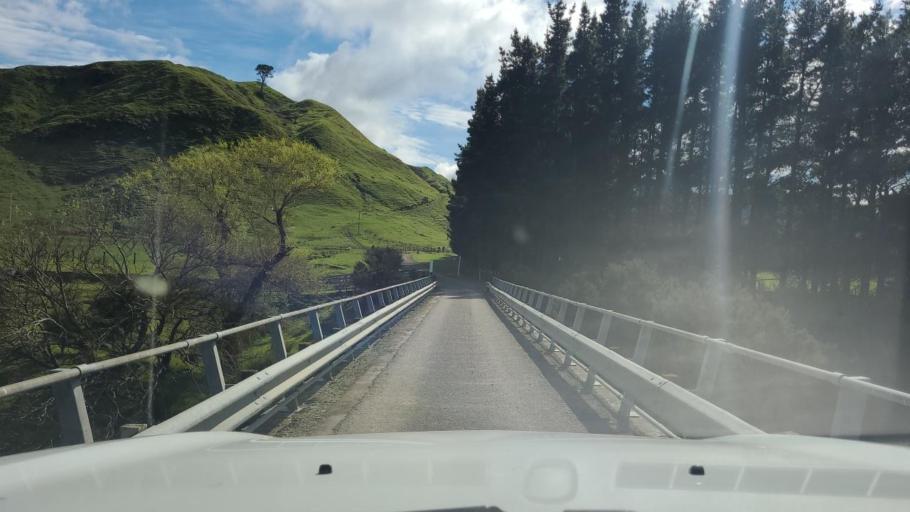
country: NZ
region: Wellington
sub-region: South Wairarapa District
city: Waipawa
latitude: -41.3766
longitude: 175.7252
